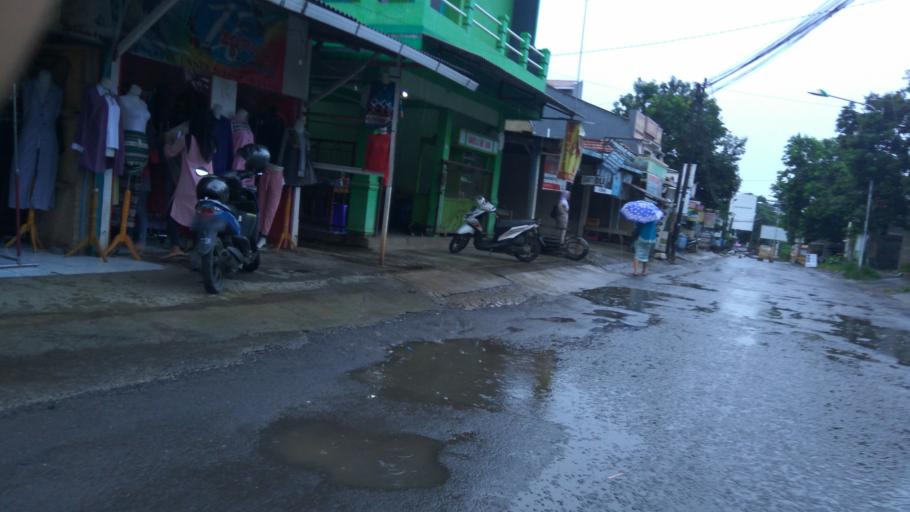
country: ID
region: Central Java
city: Semarang
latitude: -7.0453
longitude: 110.3919
